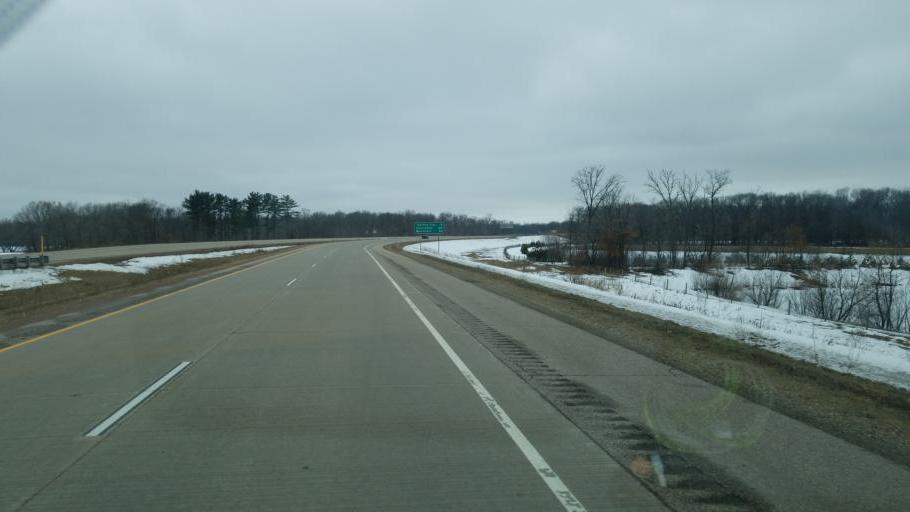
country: US
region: Wisconsin
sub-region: Portage County
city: Stevens Point
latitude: 44.5962
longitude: -89.6318
